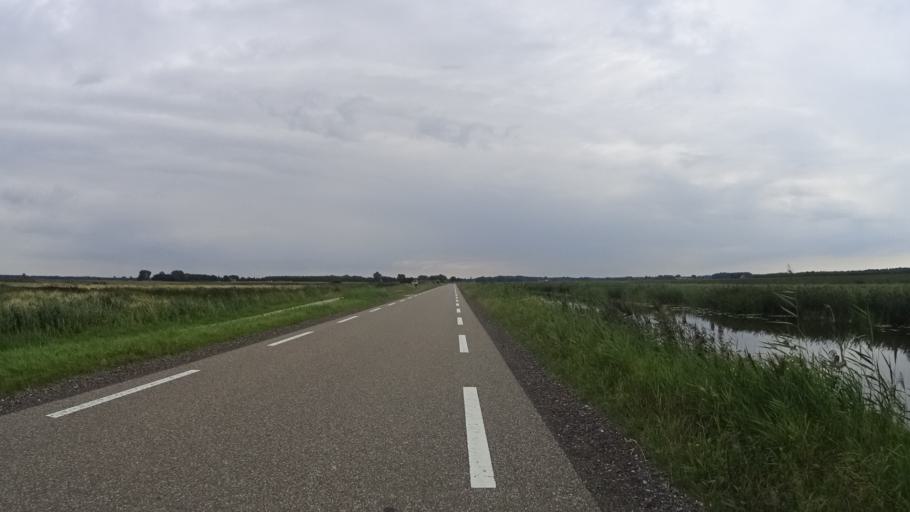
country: NL
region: Groningen
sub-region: Gemeente Slochteren
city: Slochteren
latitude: 53.2301
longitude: 6.7629
